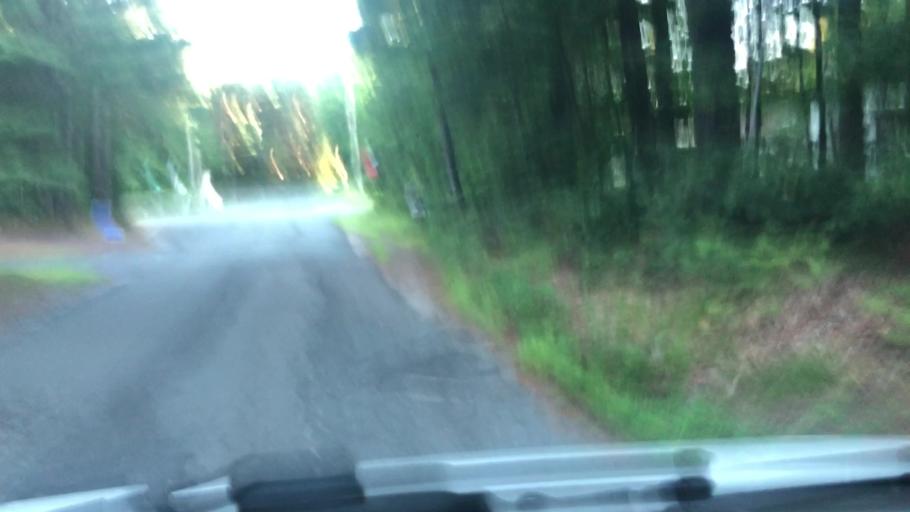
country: US
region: Massachusetts
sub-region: Hampshire County
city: Southampton
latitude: 42.2531
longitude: -72.7185
